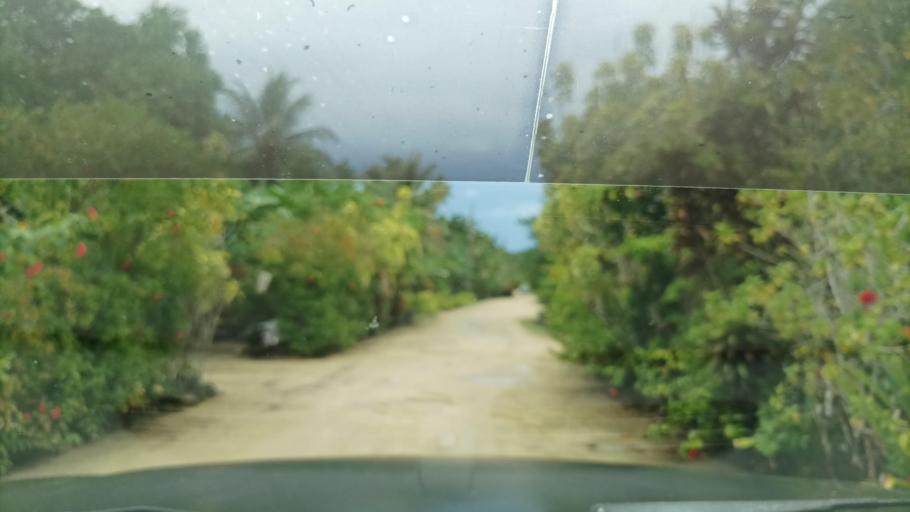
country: FM
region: Yap
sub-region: Weloy Municipality
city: Colonia
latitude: 9.5479
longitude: 138.1897
